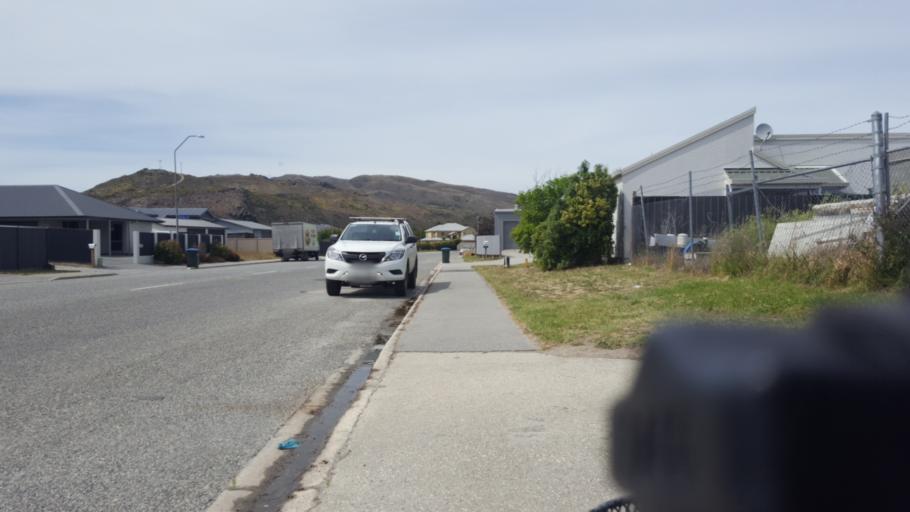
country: NZ
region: Otago
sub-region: Queenstown-Lakes District
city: Wanaka
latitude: -45.0507
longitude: 169.1954
